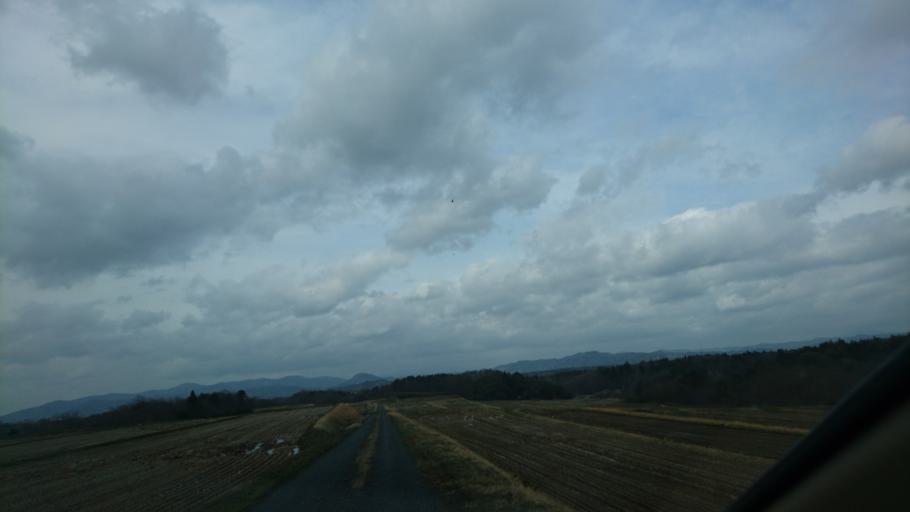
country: JP
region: Iwate
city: Ichinoseki
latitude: 38.8874
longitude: 141.1607
